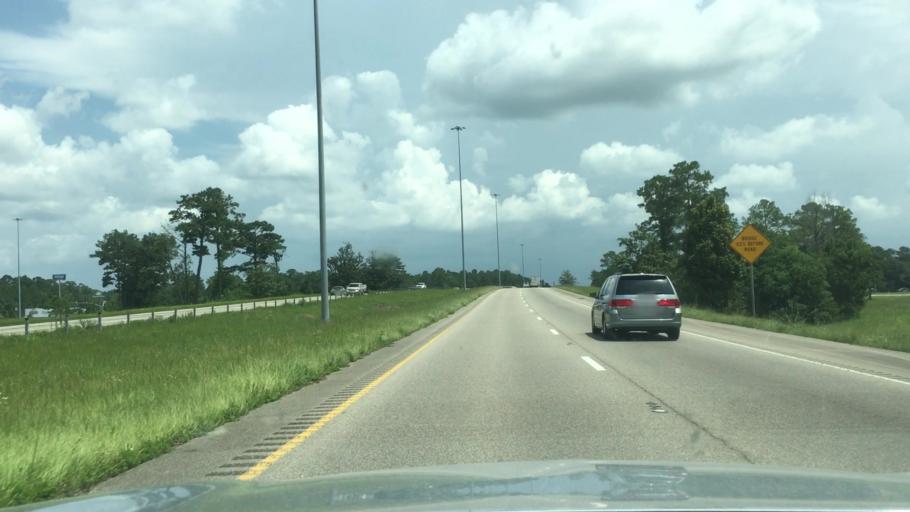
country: US
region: Mississippi
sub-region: Pearl River County
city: Picayune
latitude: 30.5149
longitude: -89.6644
